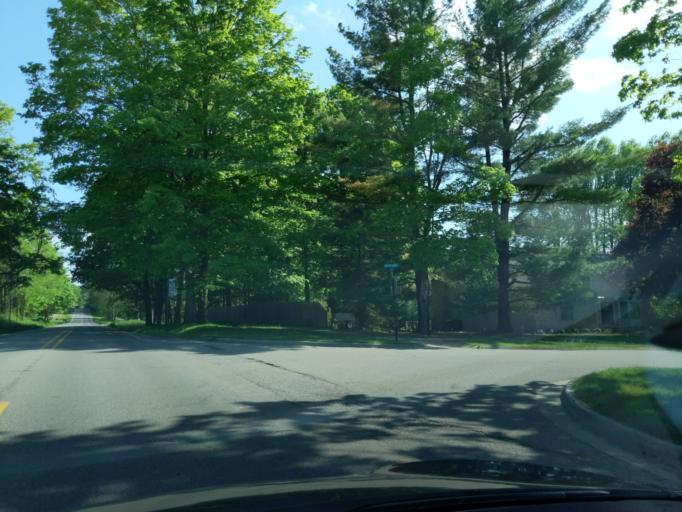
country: US
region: Michigan
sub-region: Ingham County
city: Okemos
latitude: 42.6913
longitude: -84.4104
